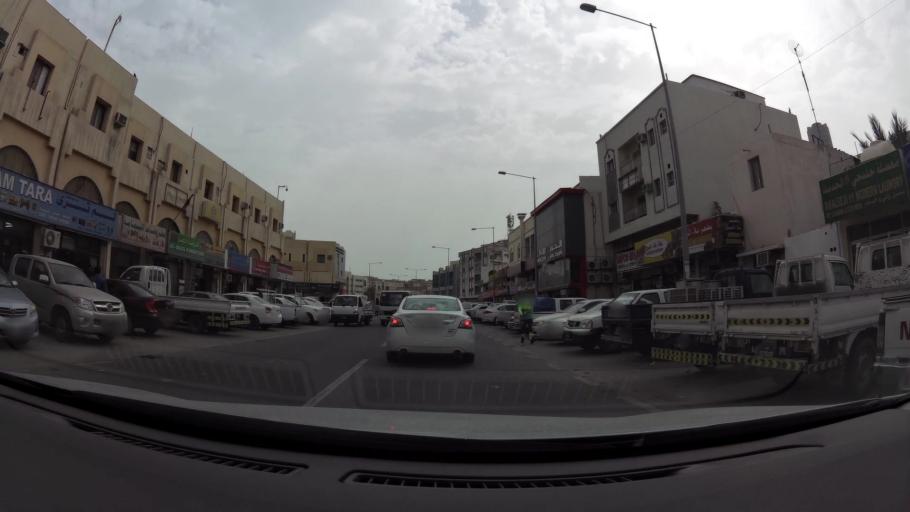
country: QA
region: Baladiyat ad Dawhah
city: Doha
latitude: 25.2696
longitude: 51.5405
